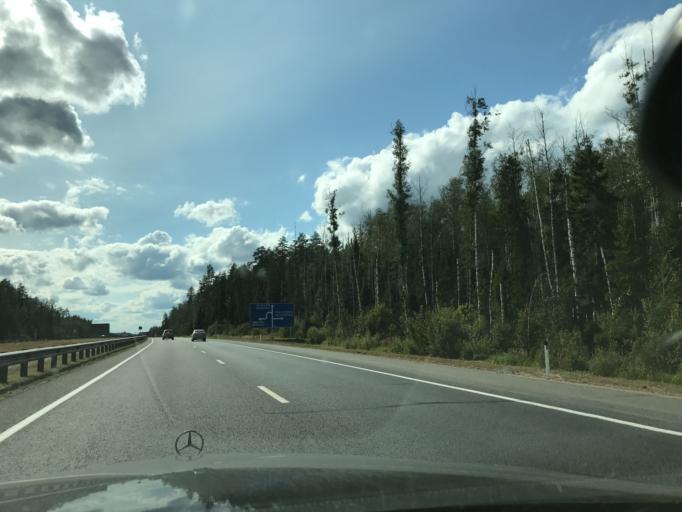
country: RU
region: Vladimir
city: Sudogda
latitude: 56.1399
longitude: 40.8971
